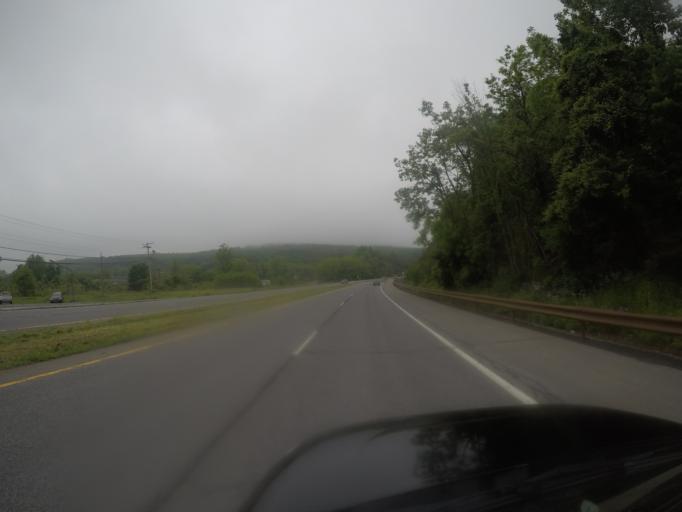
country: US
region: New York
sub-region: Ulster County
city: Hurley
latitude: 41.9498
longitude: -74.0440
